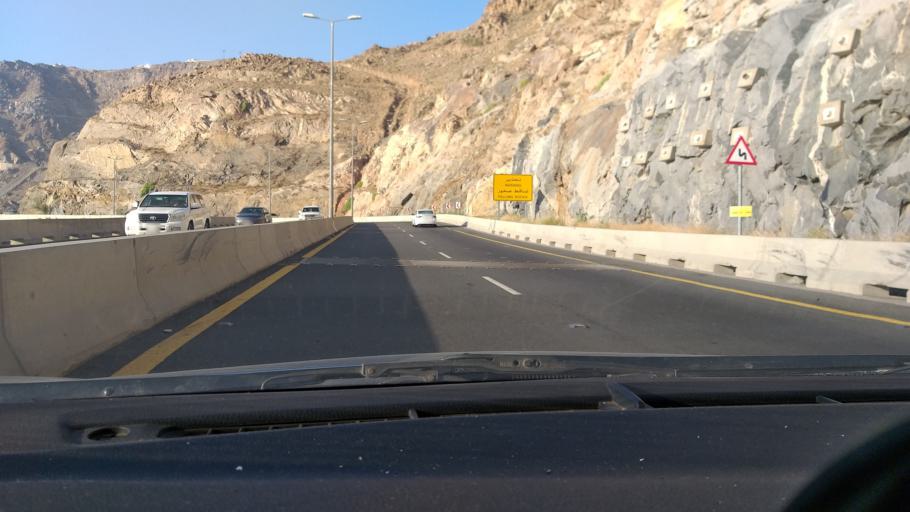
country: SA
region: Makkah
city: Al Hada
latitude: 21.3534
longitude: 40.2536
